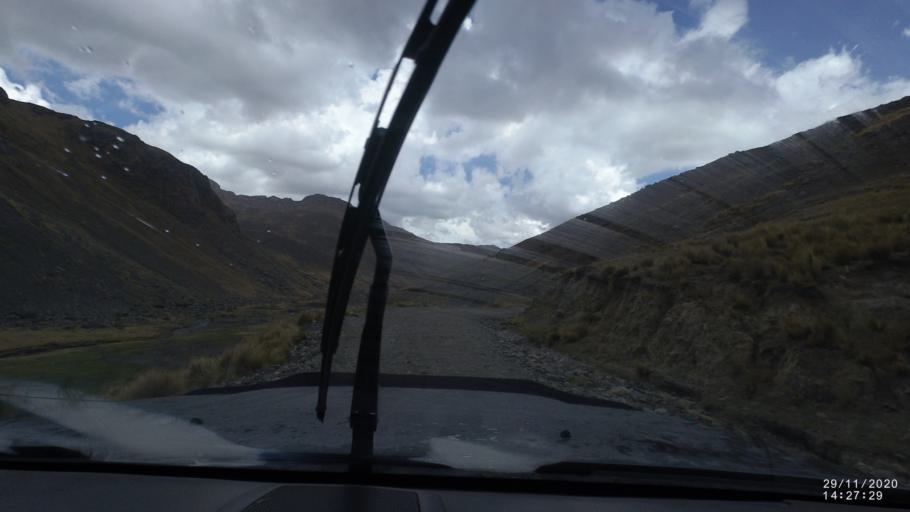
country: BO
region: Cochabamba
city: Sipe Sipe
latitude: -17.2588
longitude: -66.3656
